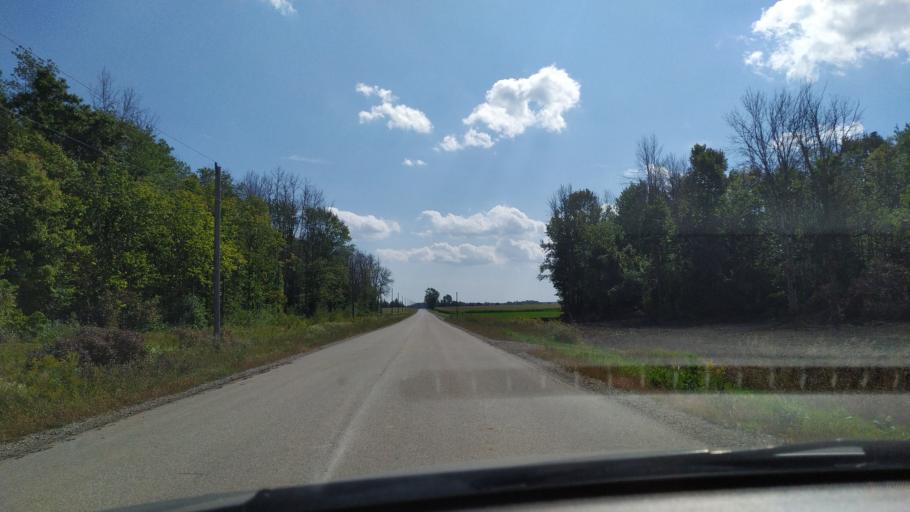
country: CA
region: Ontario
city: Stratford
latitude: 43.3076
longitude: -80.9468
